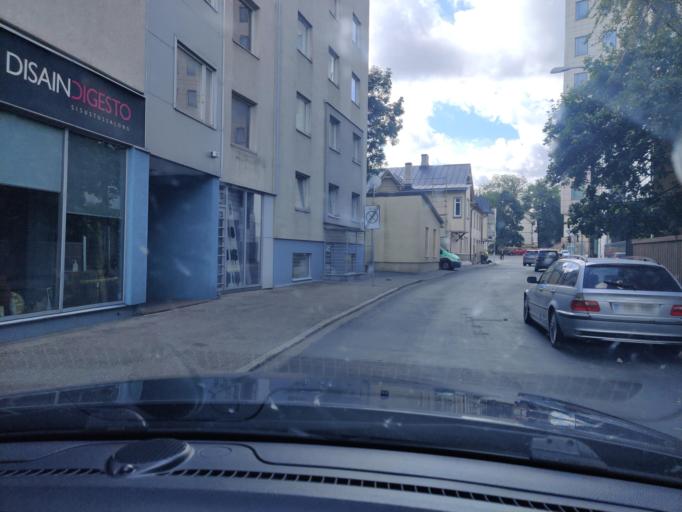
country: EE
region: Harju
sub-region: Tallinna linn
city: Tallinn
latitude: 59.4291
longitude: 24.7502
